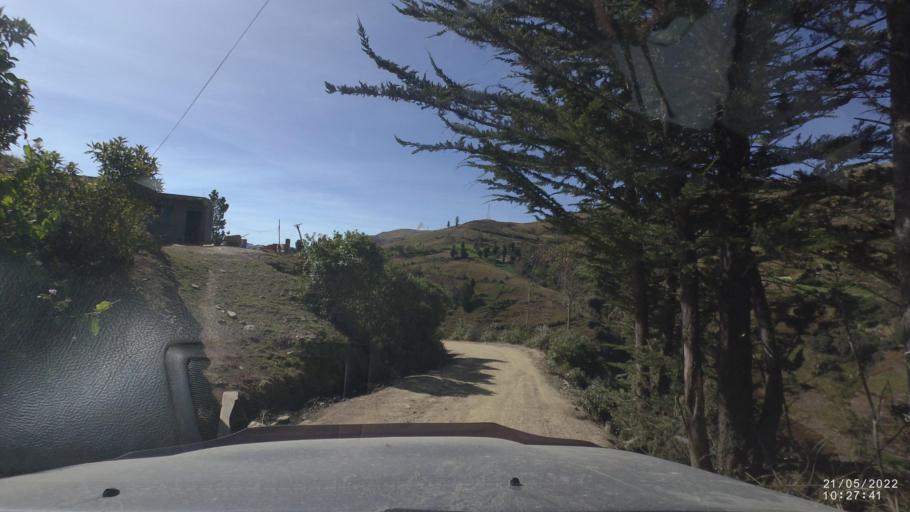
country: BO
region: Cochabamba
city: Colomi
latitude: -17.3231
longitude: -65.9435
